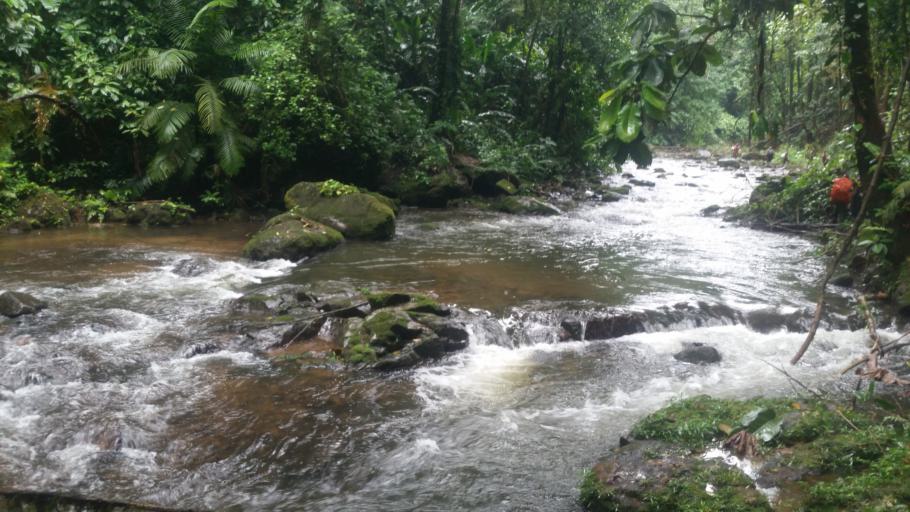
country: NI
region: Atlantico Norte (RAAN)
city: Bonanza
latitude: 14.0230
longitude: -84.7570
